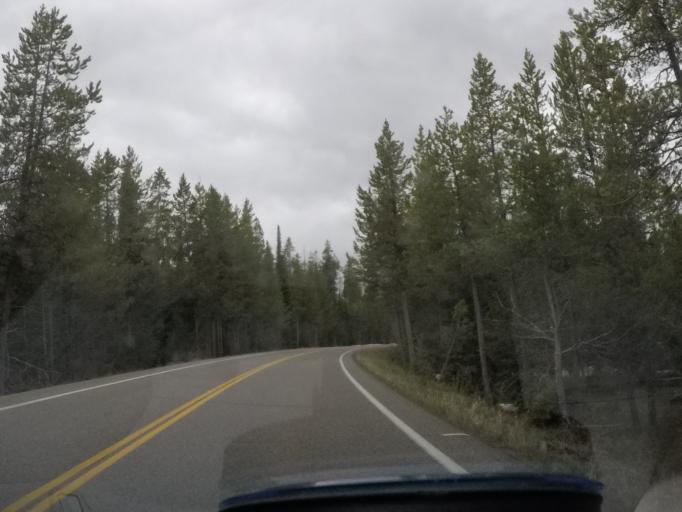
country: US
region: Wyoming
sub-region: Teton County
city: Moose Wilson Road
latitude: 43.9453
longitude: -110.6327
